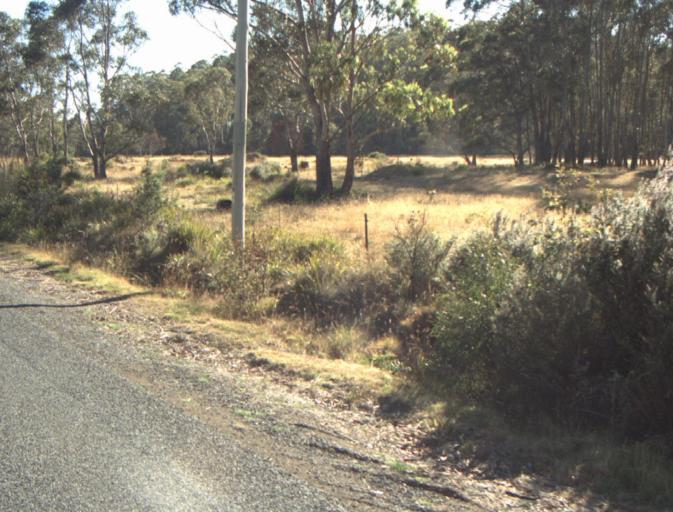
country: AU
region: Tasmania
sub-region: Launceston
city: Newstead
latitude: -41.3731
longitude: 147.2975
